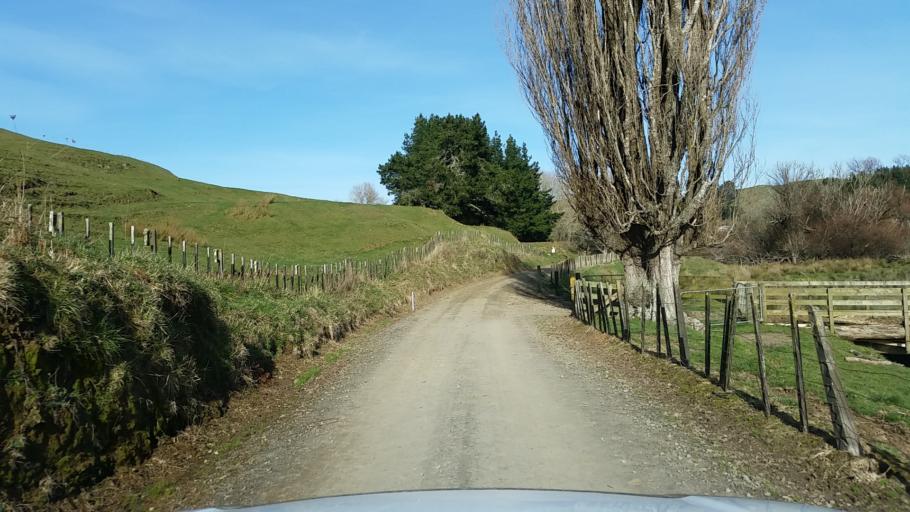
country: NZ
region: Taranaki
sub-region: South Taranaki District
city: Eltham
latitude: -39.3170
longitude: 174.5336
